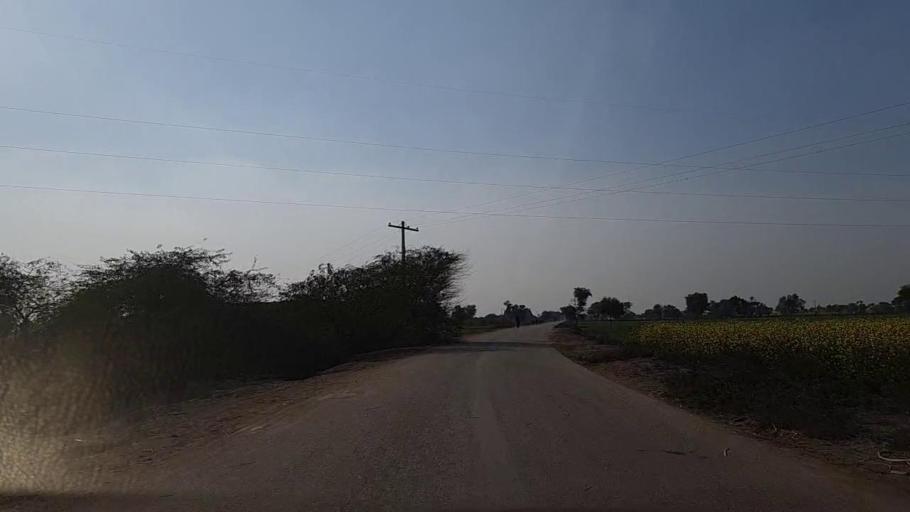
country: PK
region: Sindh
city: Daur
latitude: 26.4040
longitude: 68.3125
